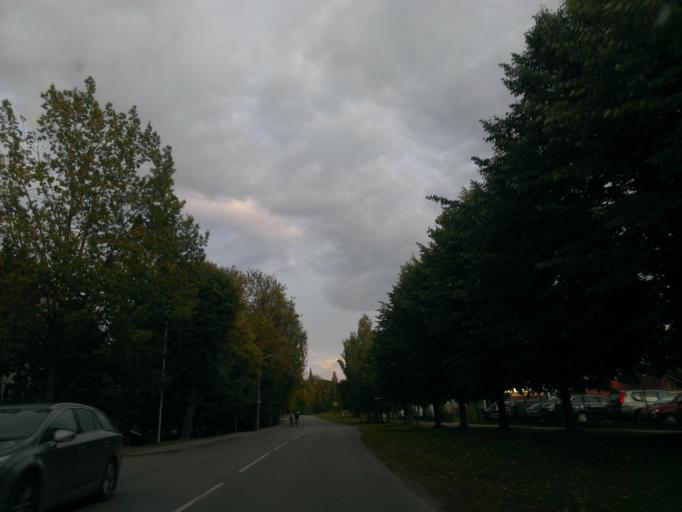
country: LV
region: Ogre
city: Ogre
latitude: 56.8194
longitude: 24.5943
